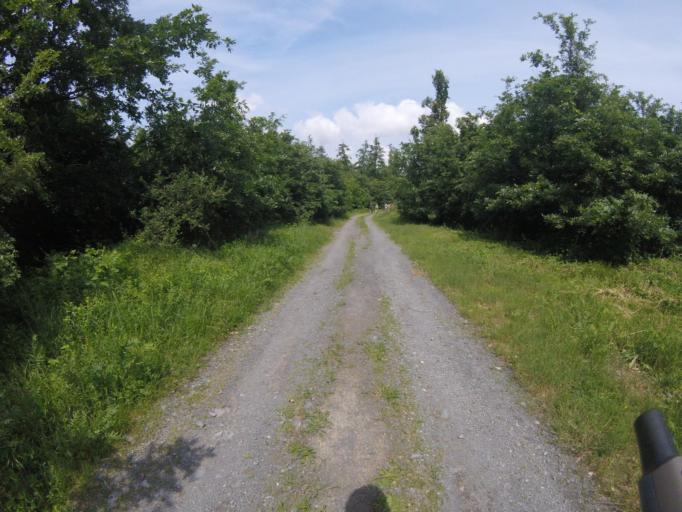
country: HU
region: Zala
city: Turje
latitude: 46.9125
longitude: 17.1817
